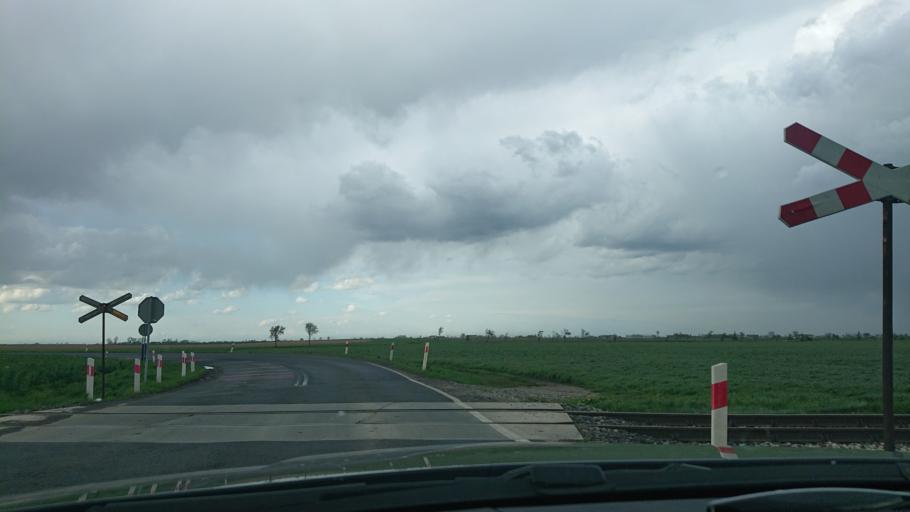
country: PL
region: Greater Poland Voivodeship
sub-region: Powiat gnieznienski
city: Gniezno
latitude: 52.5691
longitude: 17.5232
